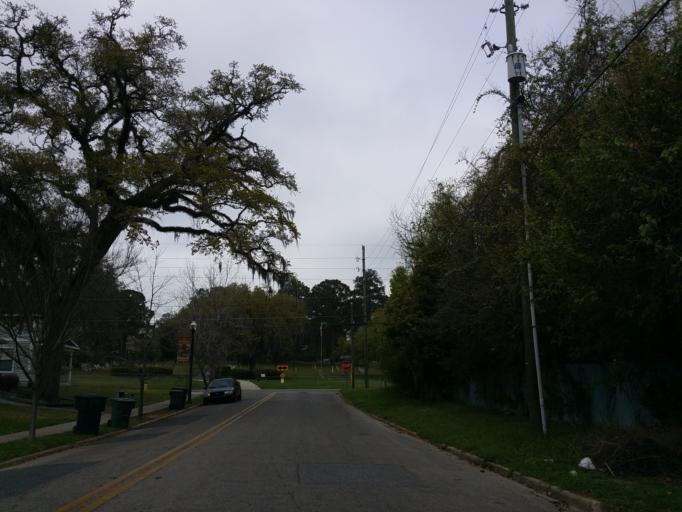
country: US
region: Florida
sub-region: Leon County
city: Tallahassee
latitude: 30.4485
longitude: -84.2856
